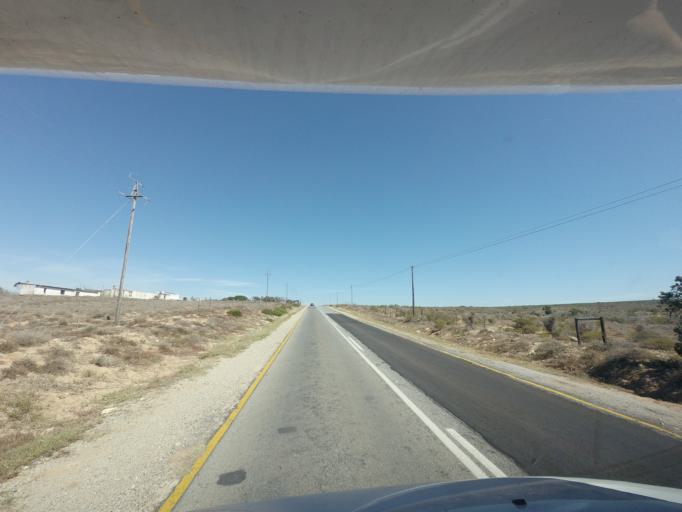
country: ZA
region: Western Cape
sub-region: West Coast District Municipality
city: Vredenburg
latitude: -32.8208
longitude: 17.9027
